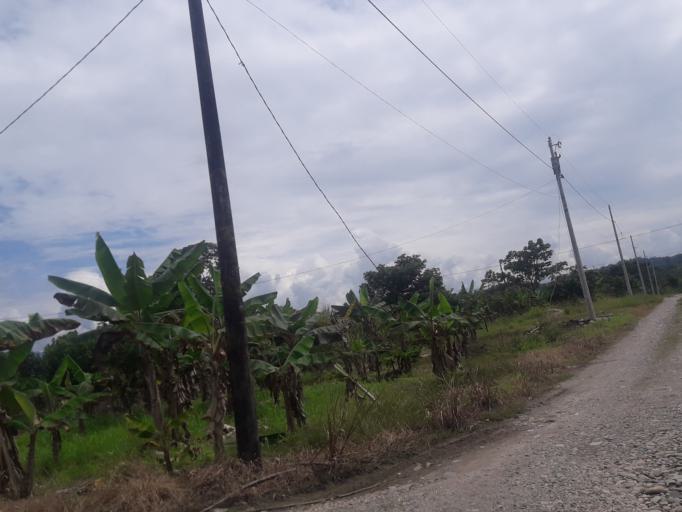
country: EC
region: Napo
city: Tena
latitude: -1.0600
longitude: -77.7958
